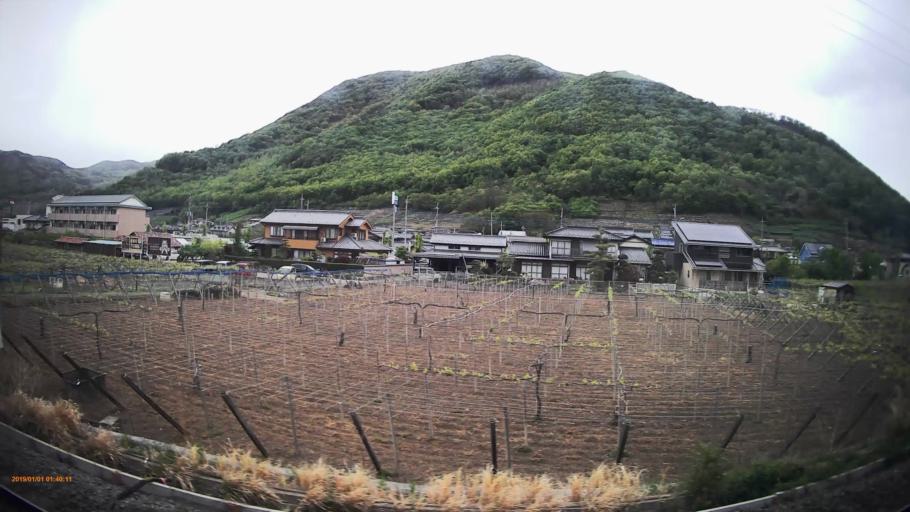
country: JP
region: Yamanashi
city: Isawa
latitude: 35.6572
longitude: 138.6260
